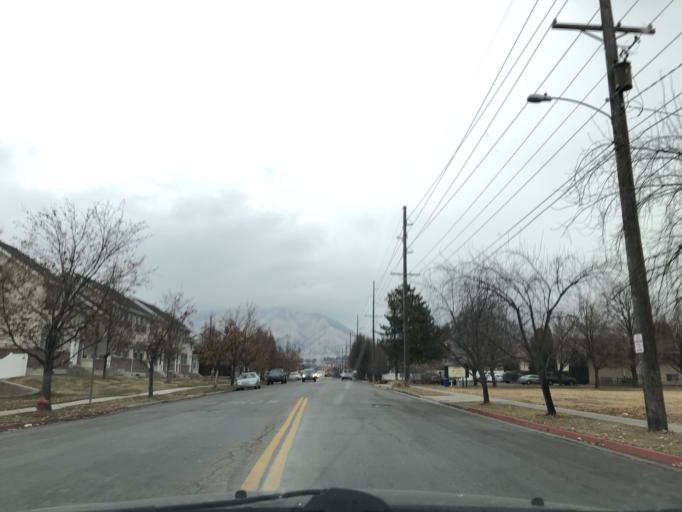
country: US
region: Utah
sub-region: Cache County
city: Logan
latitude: 41.7502
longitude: -111.8390
